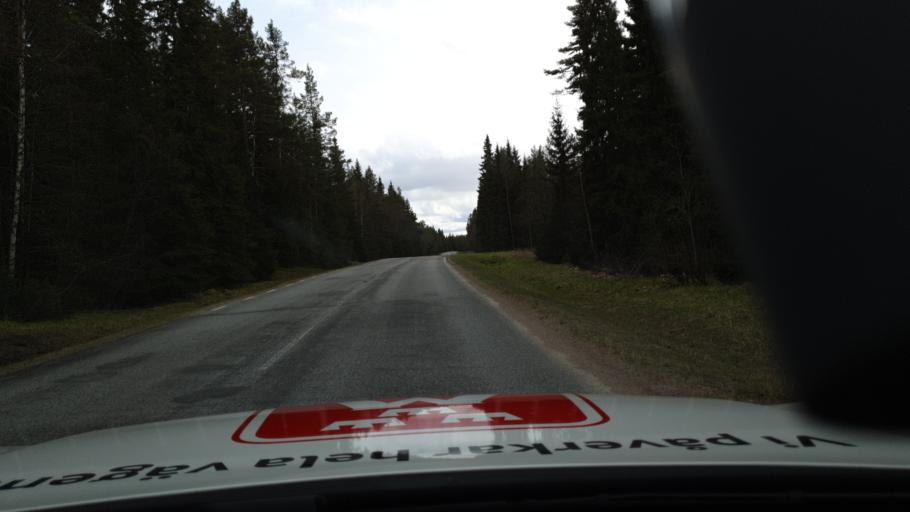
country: SE
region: Jaemtland
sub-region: Braecke Kommun
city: Braecke
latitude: 62.7876
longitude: 15.4753
